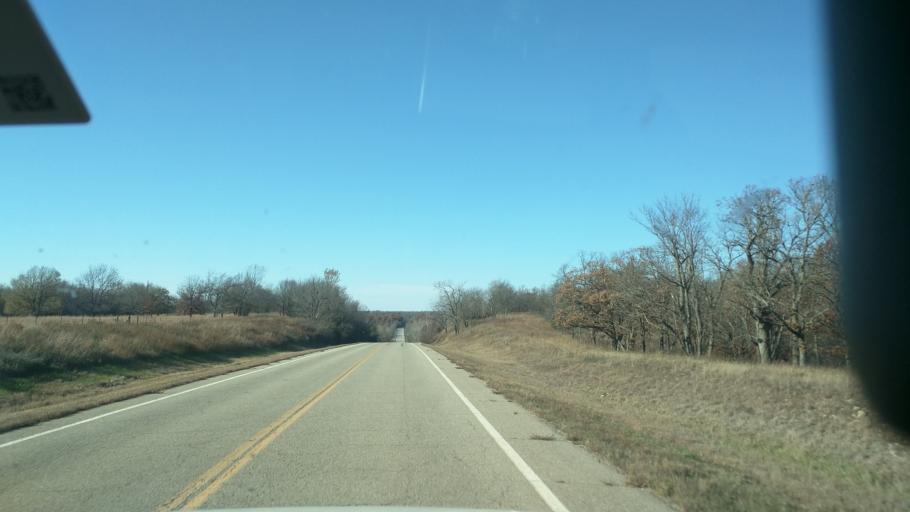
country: US
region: Oklahoma
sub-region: Nowata County
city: Nowata
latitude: 36.7441
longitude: -95.5253
